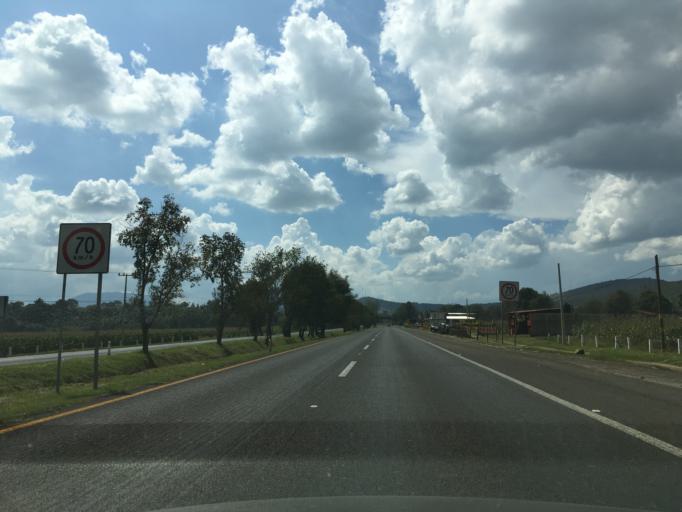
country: MX
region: Michoacan
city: Huiramba
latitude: 19.5463
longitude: -101.4451
